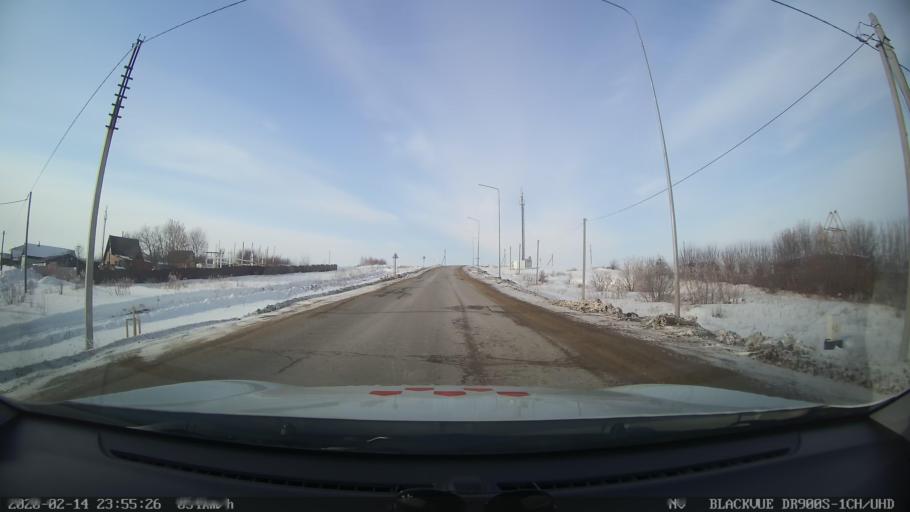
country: RU
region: Tatarstan
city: Kuybyshevskiy Zaton
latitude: 55.3167
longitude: 49.1430
